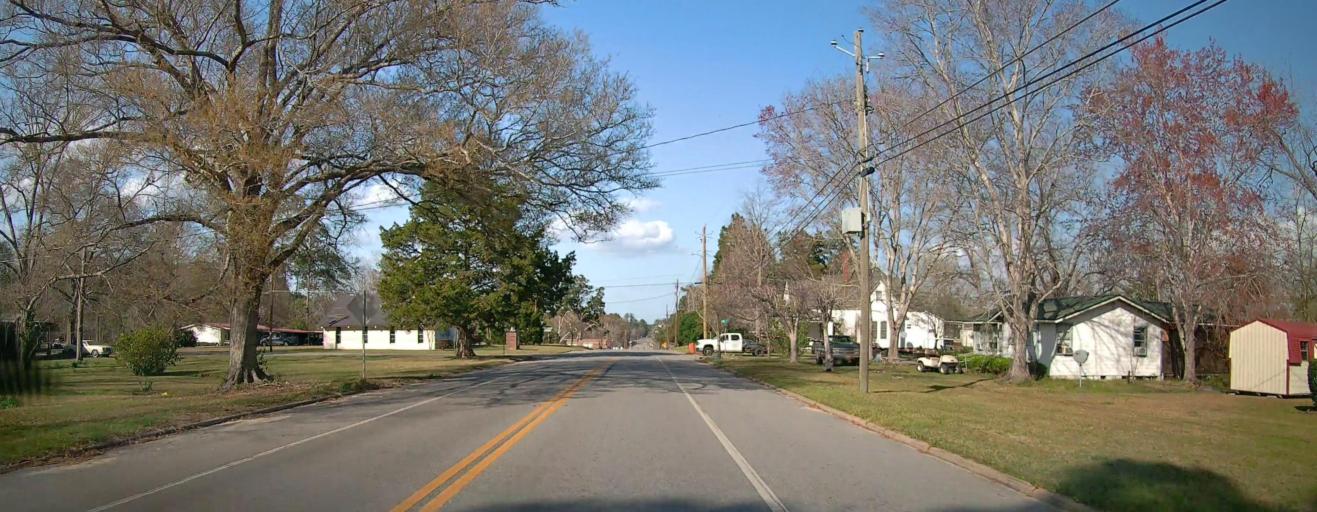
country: US
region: Georgia
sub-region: Telfair County
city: McRae
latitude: 32.0474
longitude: -82.8180
